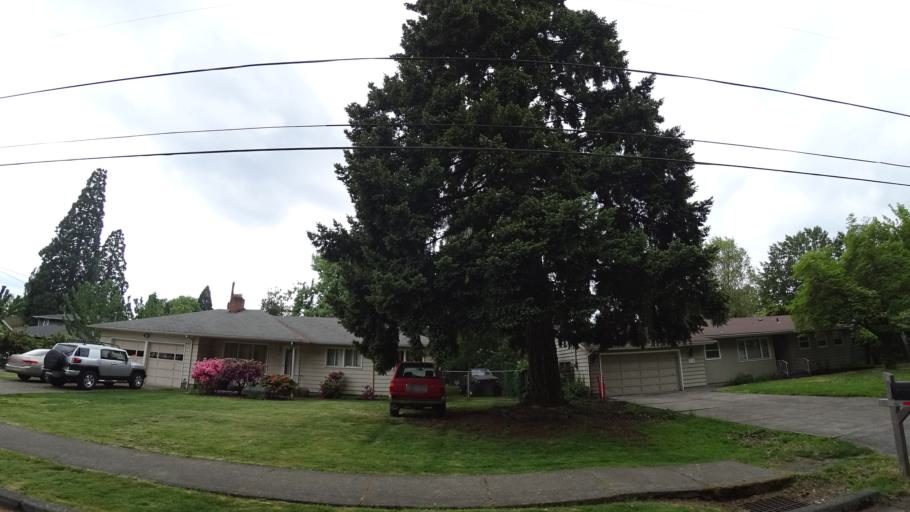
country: US
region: Oregon
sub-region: Washington County
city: Cedar Hills
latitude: 45.4952
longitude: -122.7895
